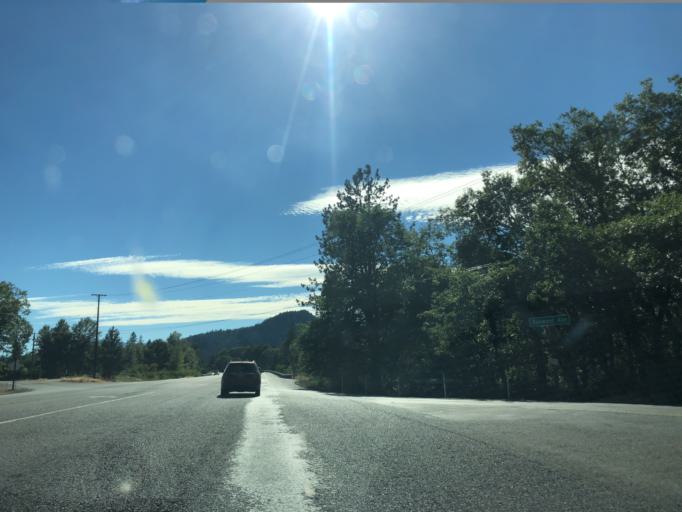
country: US
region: Oregon
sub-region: Josephine County
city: Redwood
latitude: 42.4109
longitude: -123.4259
